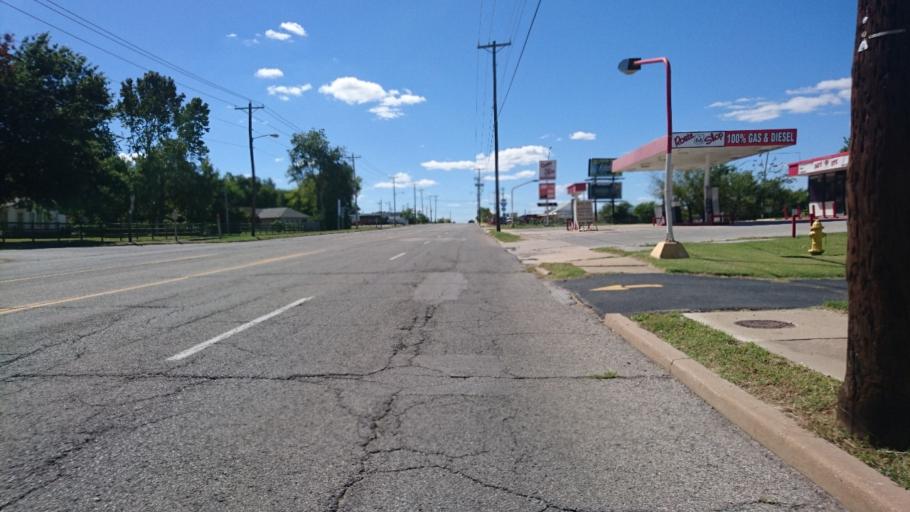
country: US
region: Oklahoma
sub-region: Tulsa County
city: Tulsa
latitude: 36.1068
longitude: -96.0178
